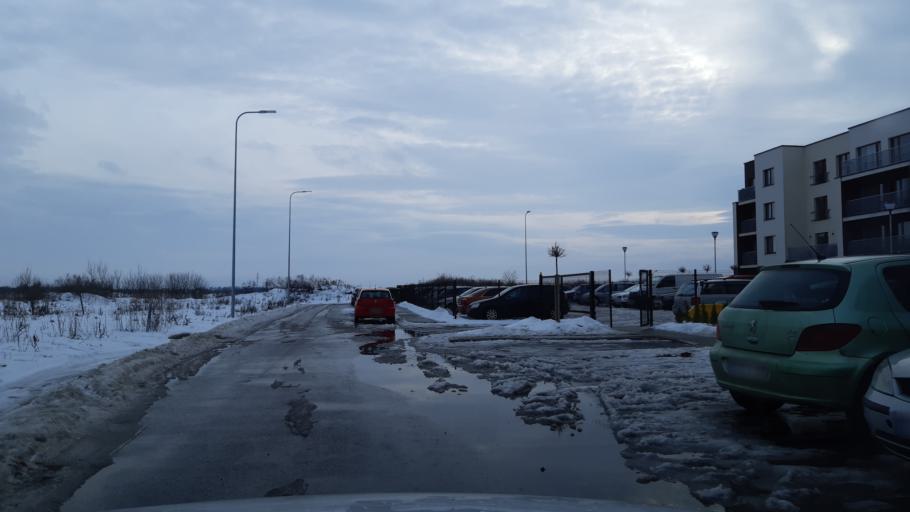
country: LT
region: Kauno apskritis
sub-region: Kauno rajonas
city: Garliava
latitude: 54.8372
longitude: 23.9059
